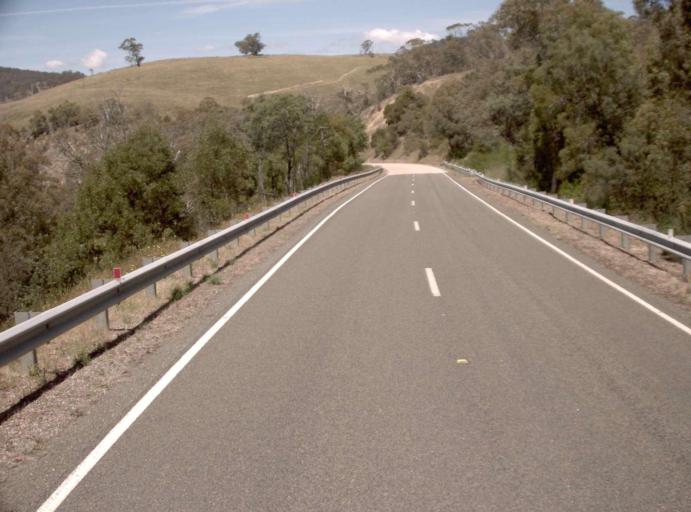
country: AU
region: Victoria
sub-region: Alpine
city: Mount Beauty
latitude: -37.1548
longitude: 147.6522
